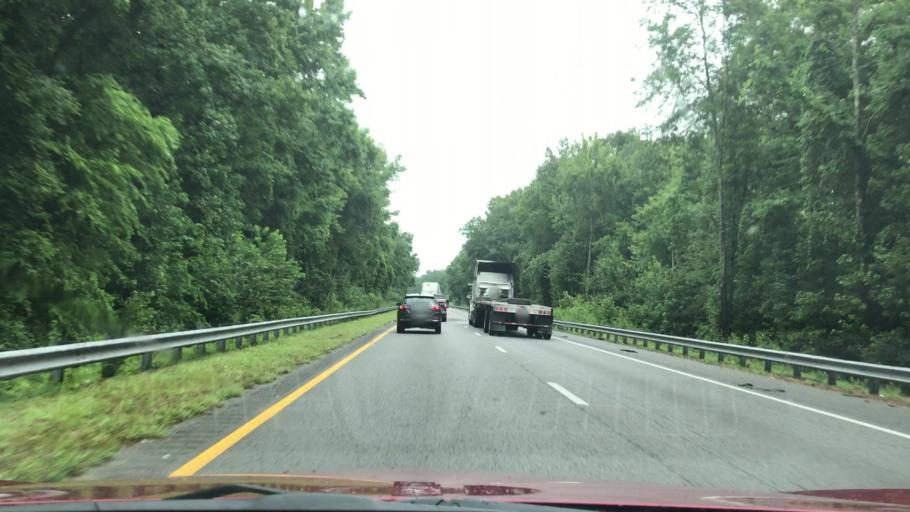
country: US
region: South Carolina
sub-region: Dorchester County
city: Ridgeville
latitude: 33.0968
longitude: -80.2367
